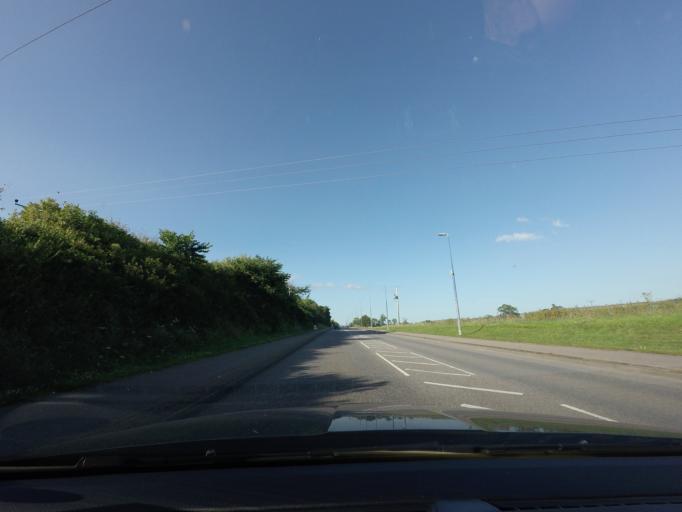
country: GB
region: Scotland
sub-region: Highland
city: Dingwall
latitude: 57.5820
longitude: -4.4346
